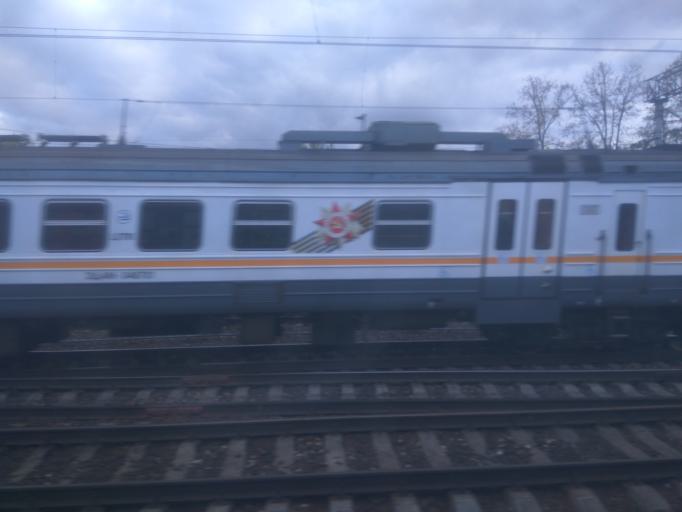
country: RU
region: Moscow
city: Solntsevo
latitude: 55.6559
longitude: 37.3760
